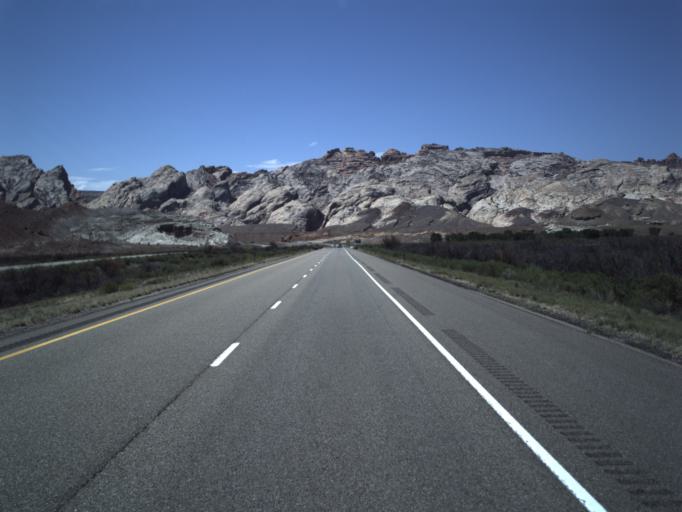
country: US
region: Utah
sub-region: Carbon County
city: East Carbon City
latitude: 38.9226
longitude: -110.3991
